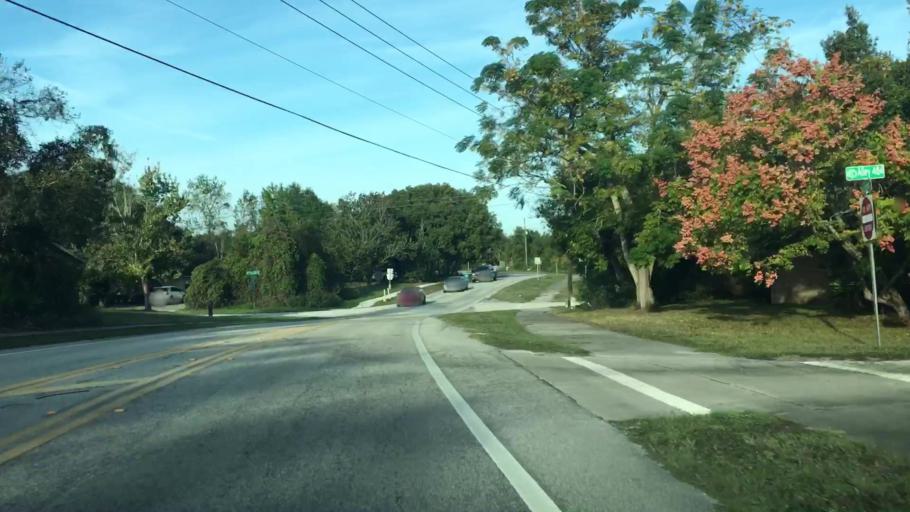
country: US
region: Florida
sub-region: Volusia County
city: Deltona
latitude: 28.9176
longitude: -81.2226
